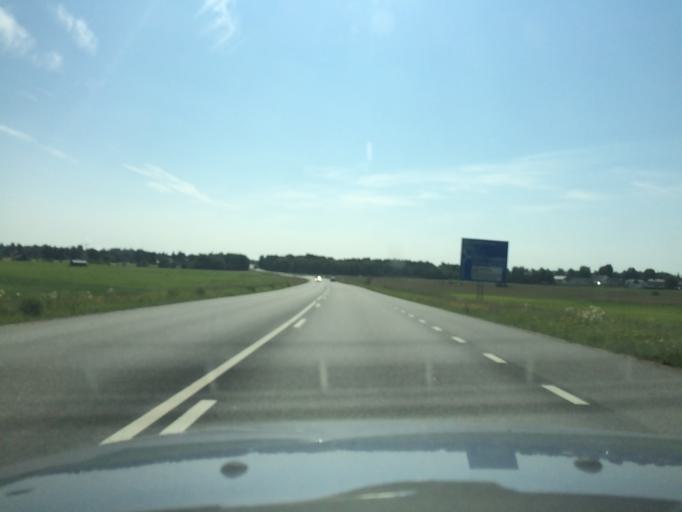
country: SE
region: Norrbotten
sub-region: Pitea Kommun
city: Bergsviken
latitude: 65.3555
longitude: 21.4015
